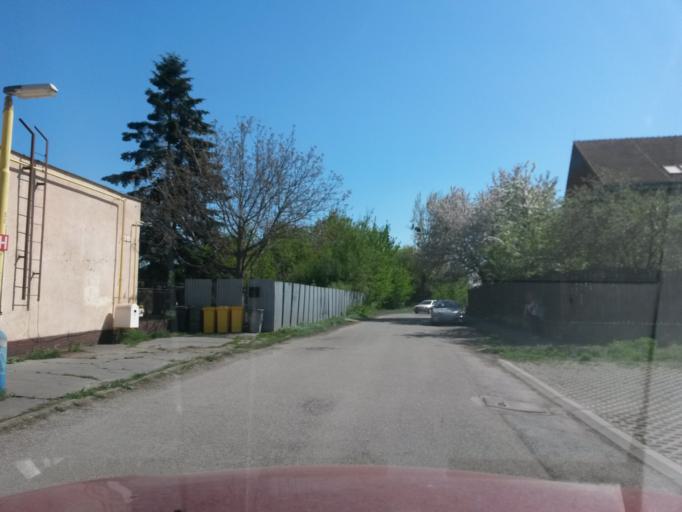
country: SK
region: Kosicky
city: Kosice
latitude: 48.6791
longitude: 21.2755
